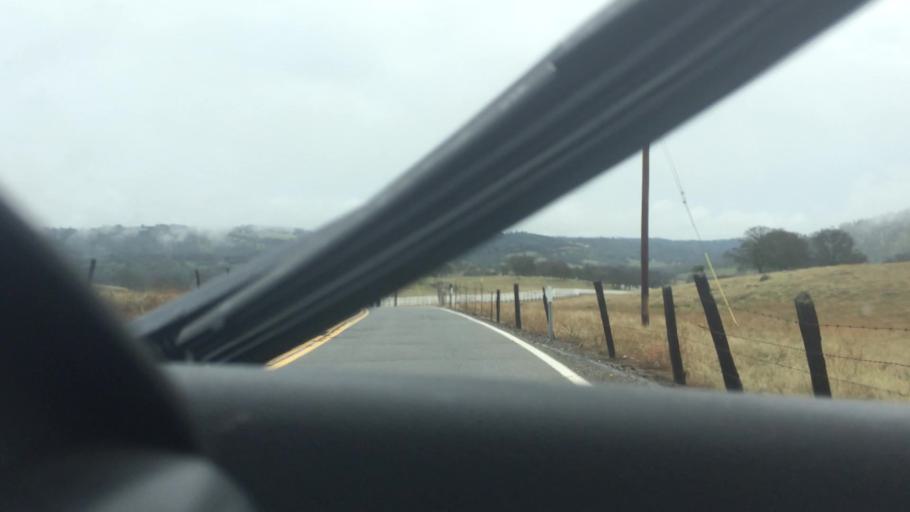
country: US
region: California
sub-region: El Dorado County
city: Cameron Park
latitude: 38.6064
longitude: -121.0338
